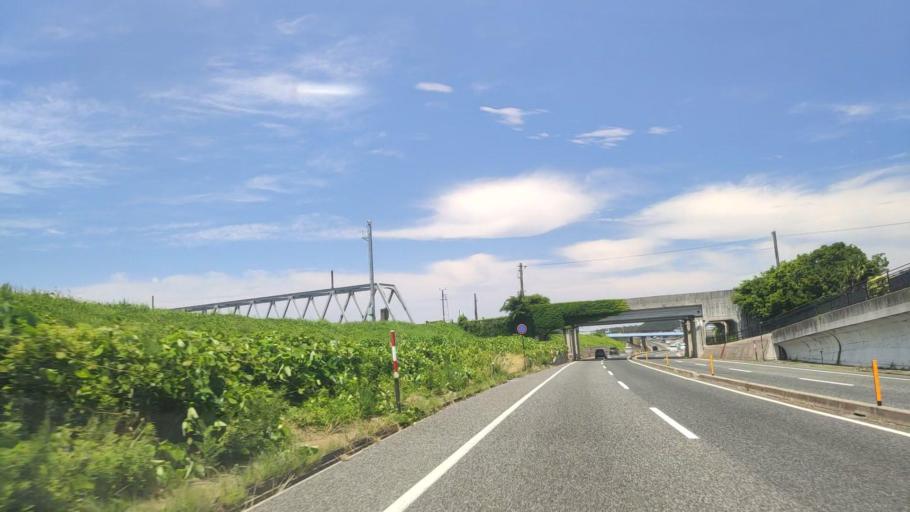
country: JP
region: Tottori
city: Tottori
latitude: 35.4969
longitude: 134.2172
